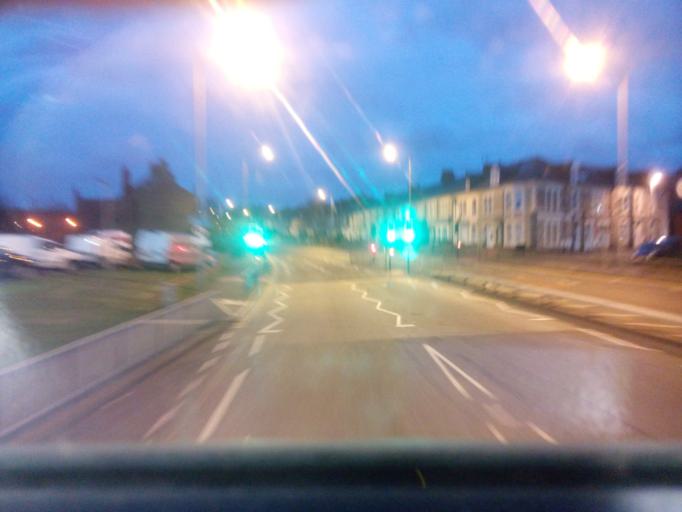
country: GB
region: England
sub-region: Gateshead
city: Gateshead
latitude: 54.9548
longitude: -1.5996
